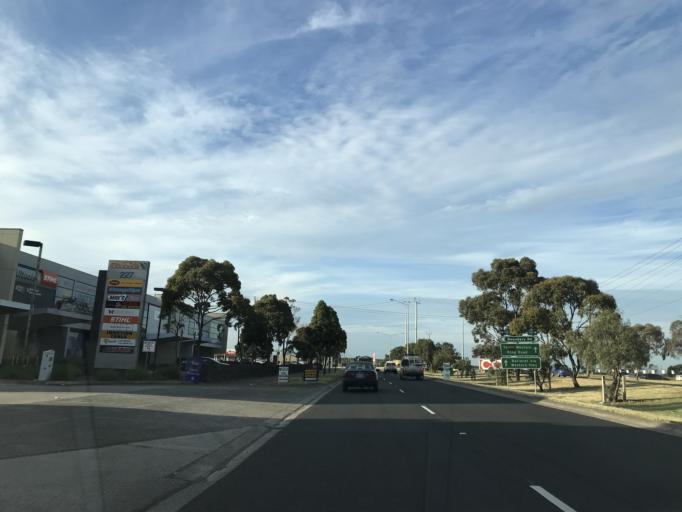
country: AU
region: Victoria
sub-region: Brimbank
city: Derrimut
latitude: -37.8150
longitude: 144.7871
